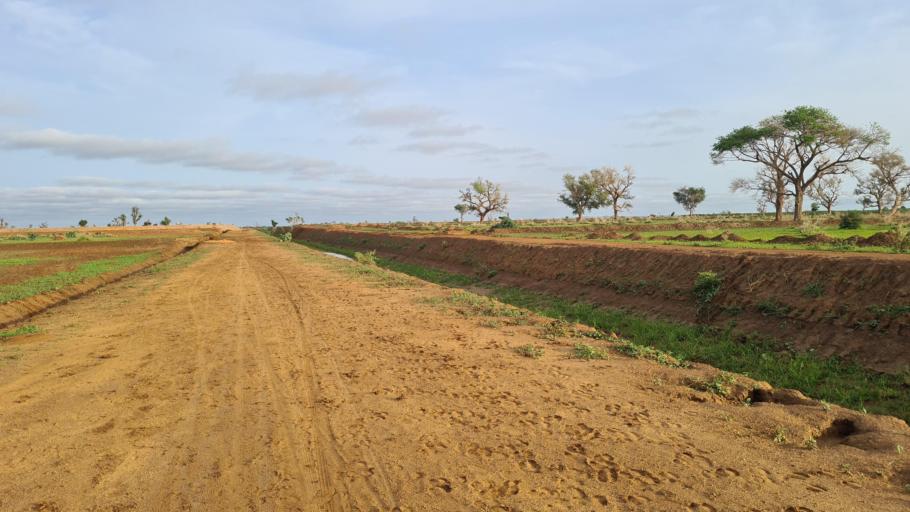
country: NE
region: Tahoua
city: Birni N Konni
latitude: 13.7873
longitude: 5.2311
